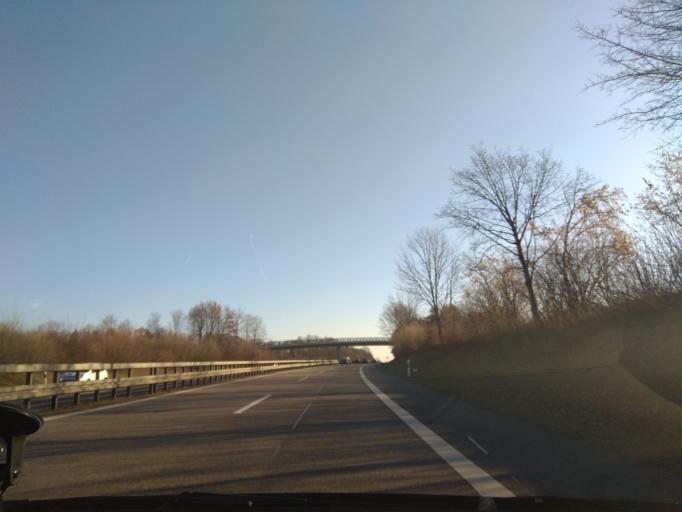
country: DE
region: Baden-Wuerttemberg
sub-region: Regierungsbezirk Stuttgart
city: Altenriet
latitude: 48.5956
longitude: 9.1751
